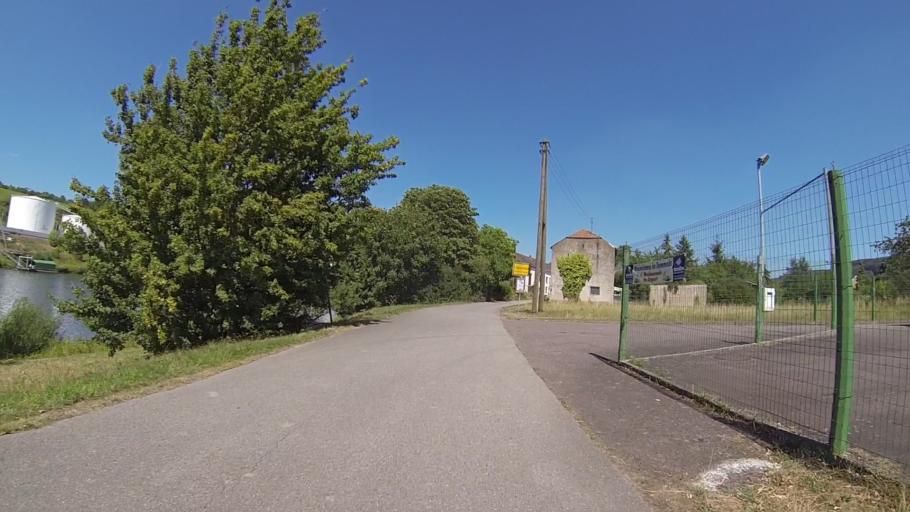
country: DE
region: Rheinland-Pfalz
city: Temmels
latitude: 49.6890
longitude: 6.4583
